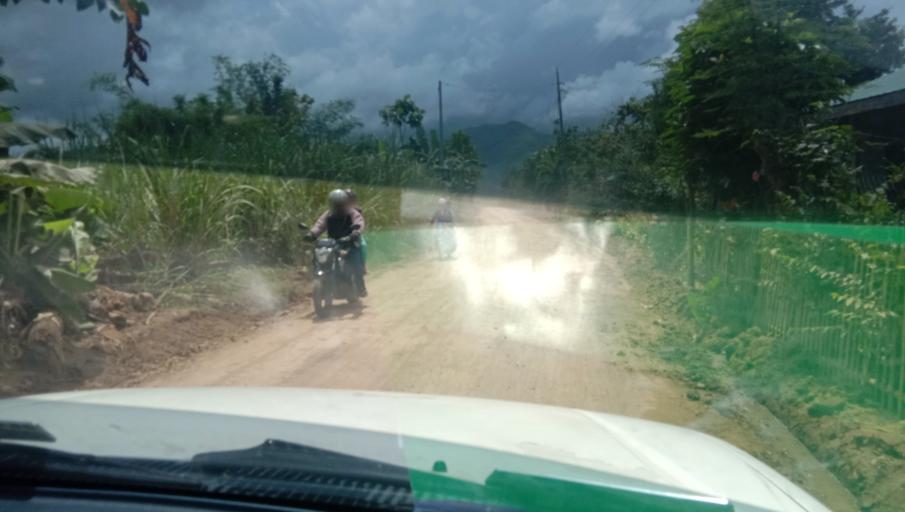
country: PH
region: Western Visayas
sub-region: Province of Iloilo
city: Balasan
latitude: 11.4693
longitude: 123.0578
